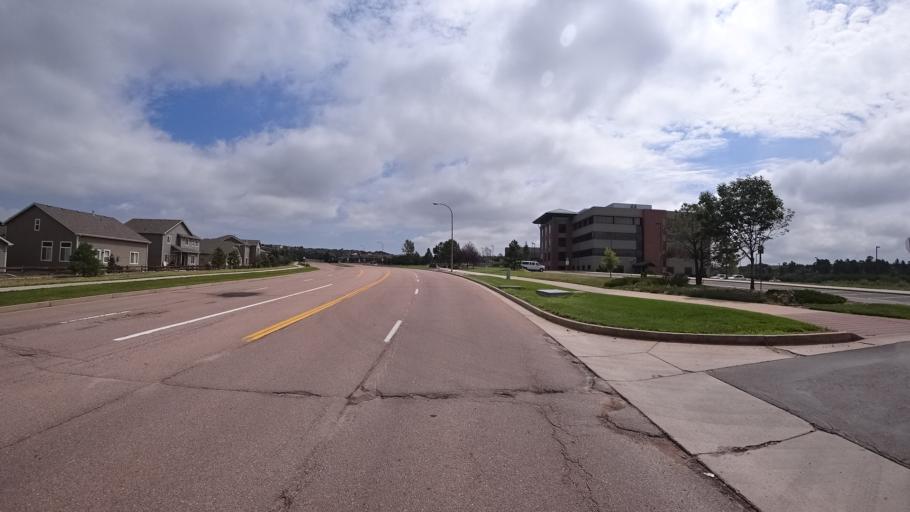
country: US
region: Colorado
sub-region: El Paso County
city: Gleneagle
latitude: 39.0094
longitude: -104.8105
